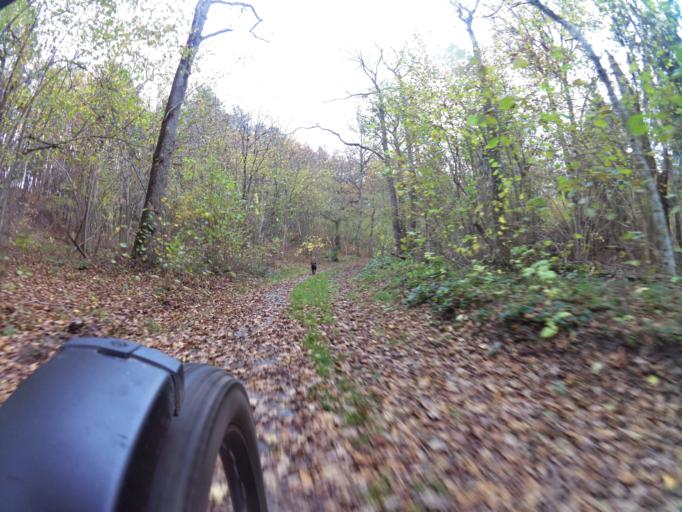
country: PL
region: Pomeranian Voivodeship
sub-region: Powiat pucki
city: Krokowa
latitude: 54.8308
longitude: 18.1146
